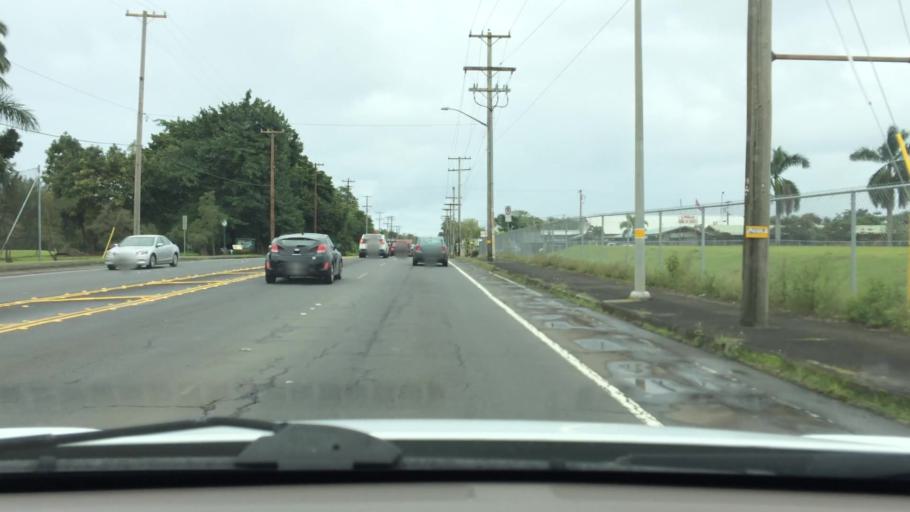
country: US
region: Hawaii
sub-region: Hawaii County
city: Hilo
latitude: 19.7225
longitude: -155.0683
